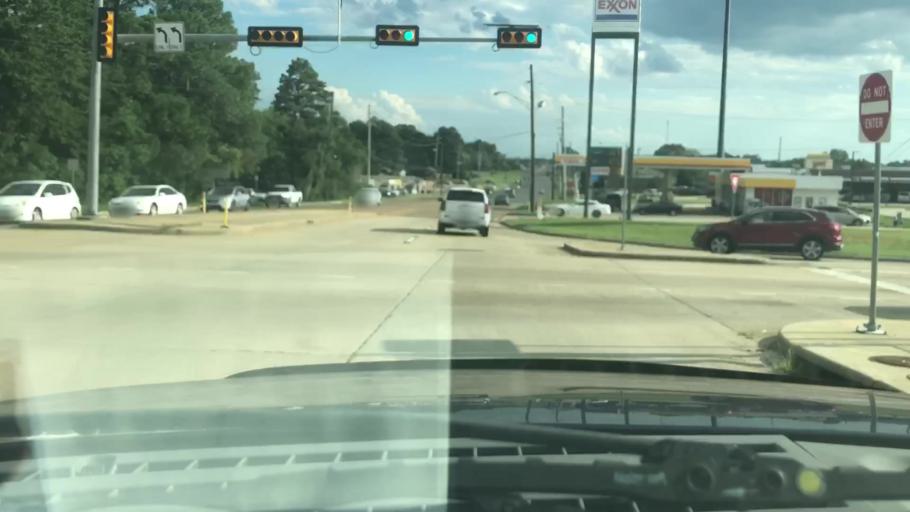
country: US
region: Arkansas
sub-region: Miller County
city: Texarkana
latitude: 33.4640
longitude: -94.0662
